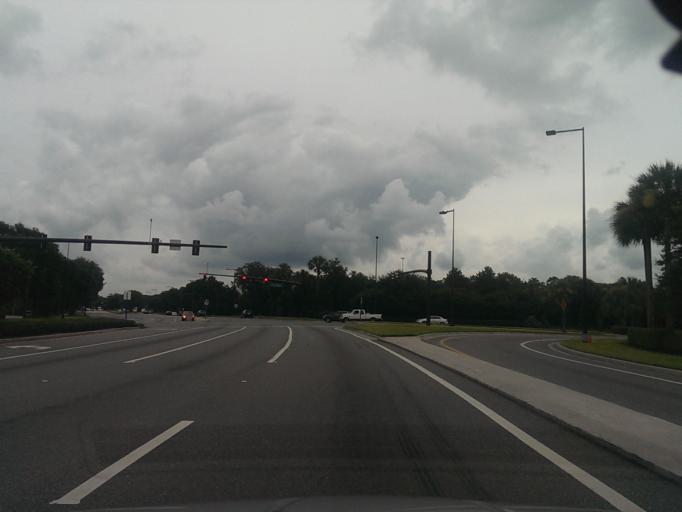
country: US
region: Florida
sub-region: Osceola County
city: Celebration
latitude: 28.3642
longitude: -81.5479
